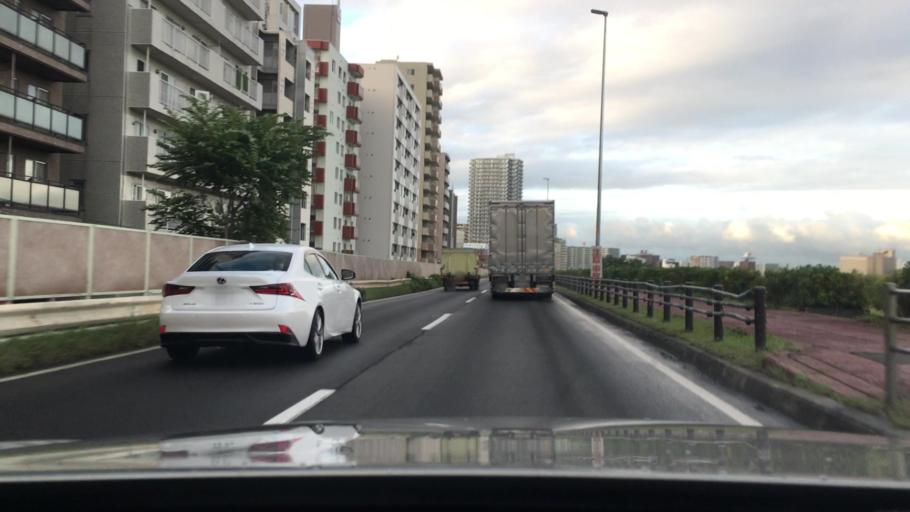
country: JP
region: Hokkaido
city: Sapporo
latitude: 43.0432
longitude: 141.3580
